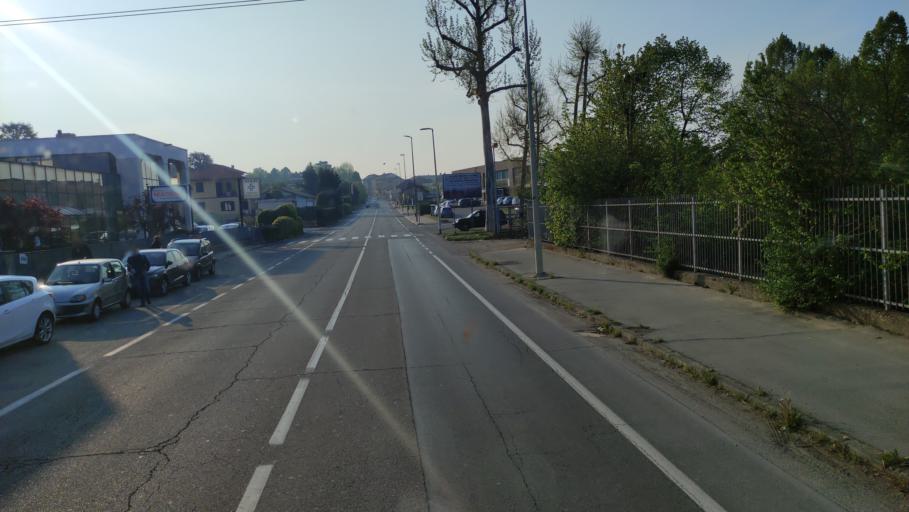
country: IT
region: Piedmont
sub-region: Provincia di Torino
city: Trofarello
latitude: 44.9876
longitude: 7.7265
